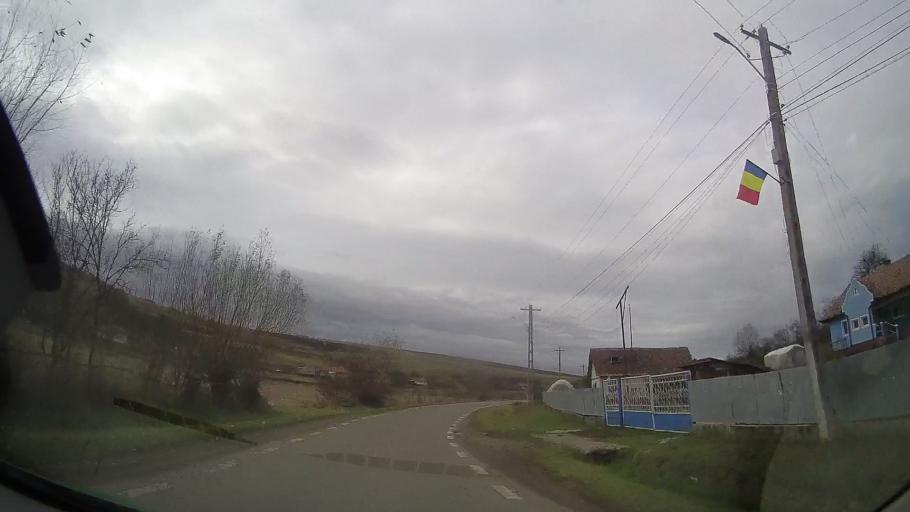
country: RO
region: Mures
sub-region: Comuna Cozma
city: Cozma
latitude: 46.8117
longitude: 24.5104
